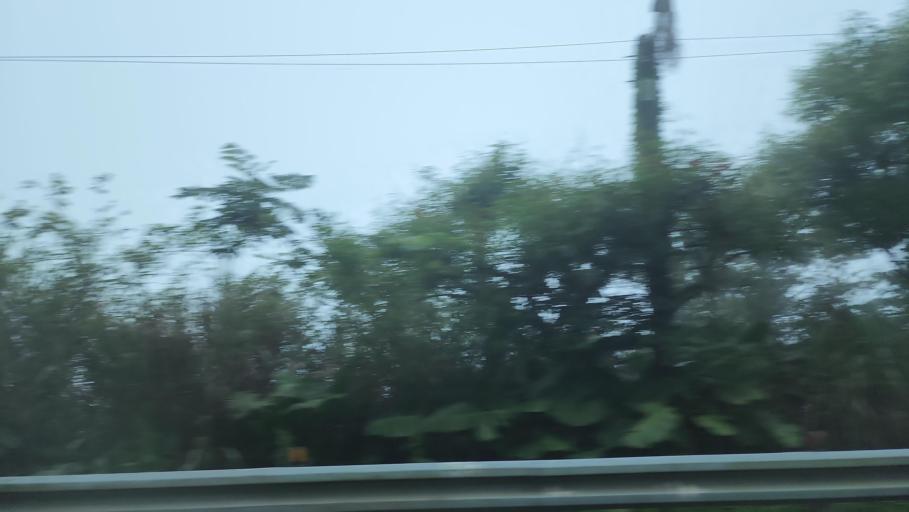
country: TW
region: Taipei
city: Taipei
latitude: 25.1386
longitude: 121.6026
